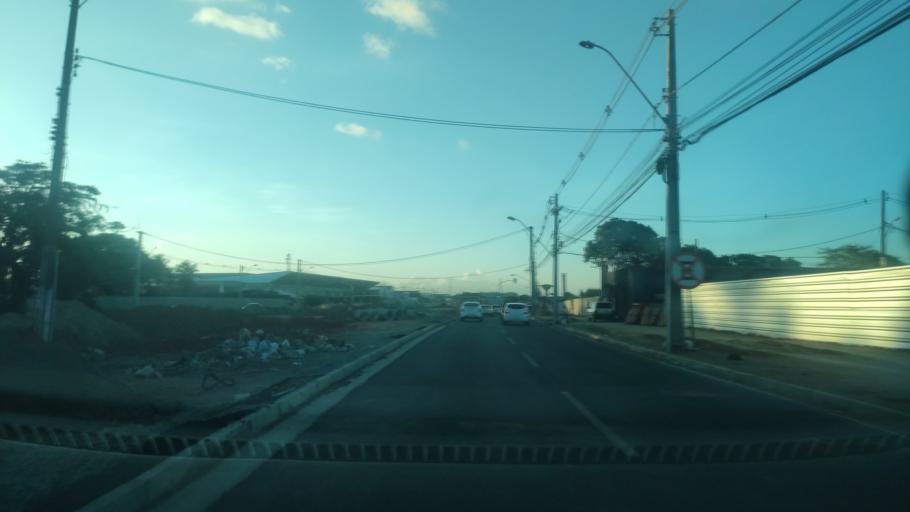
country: BR
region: Alagoas
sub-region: Satuba
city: Satuba
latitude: -9.5706
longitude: -35.7746
